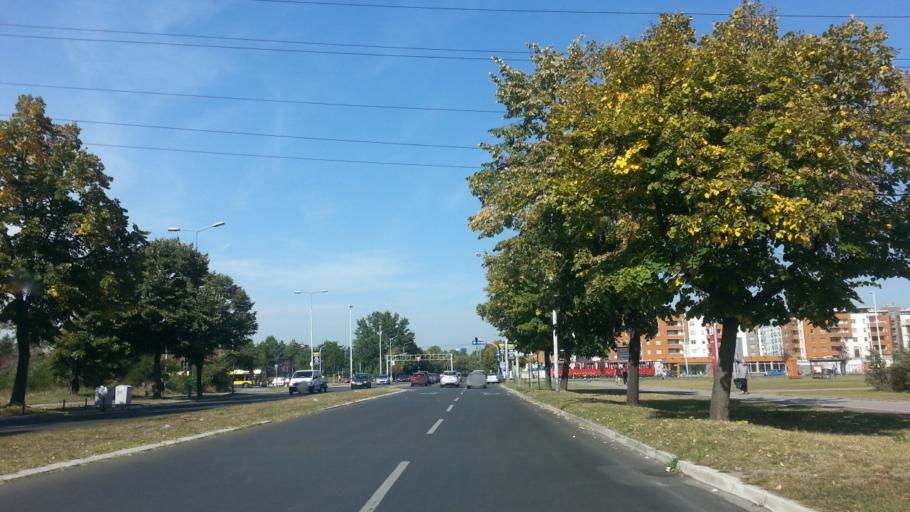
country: RS
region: Central Serbia
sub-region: Belgrade
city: Novi Beograd
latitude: 44.8033
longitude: 20.3996
